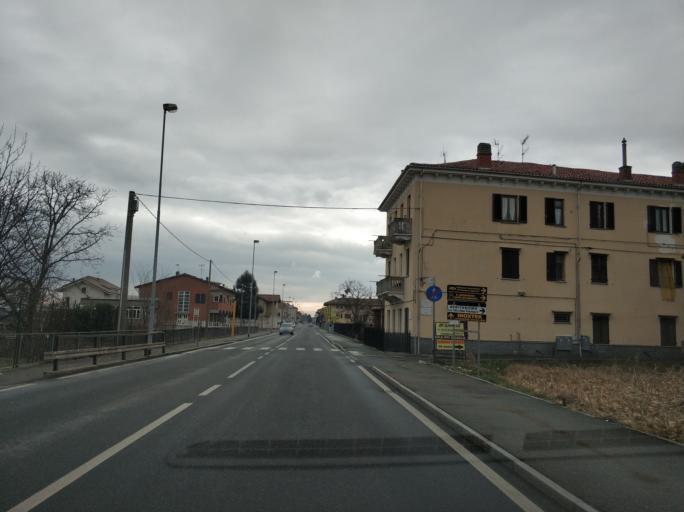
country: IT
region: Piedmont
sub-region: Provincia di Torino
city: Pavone Canavese
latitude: 45.4387
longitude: 7.8786
